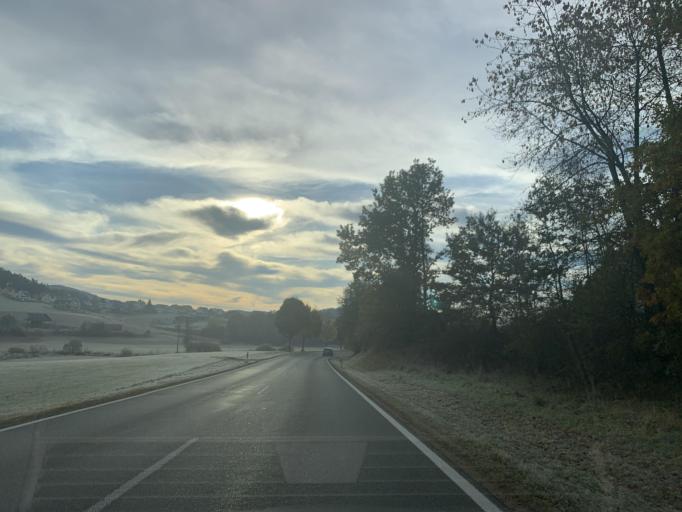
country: DE
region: Bavaria
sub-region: Upper Palatinate
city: Pettendorf
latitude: 49.3732
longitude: 12.3772
